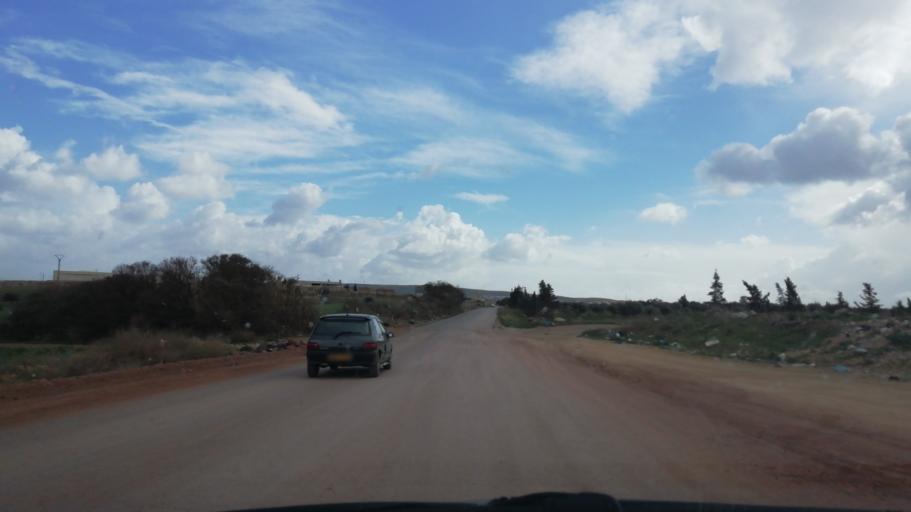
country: DZ
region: Oran
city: Sidi ech Chahmi
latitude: 35.6349
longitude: -0.5359
